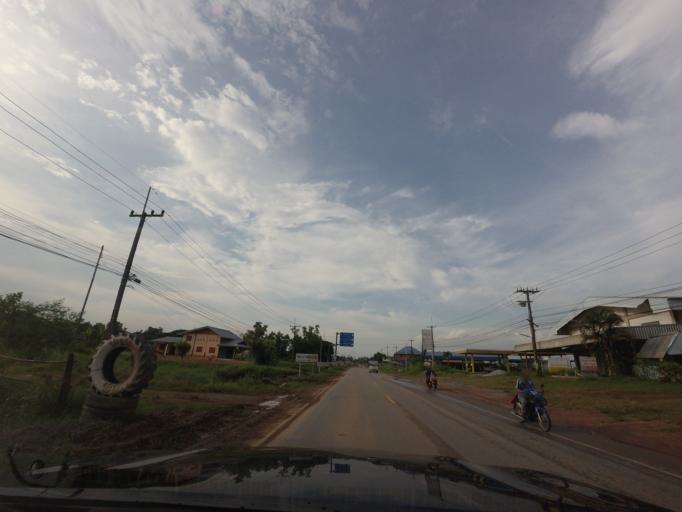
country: TH
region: Nong Khai
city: Pho Tak
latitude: 17.7733
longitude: 102.3957
